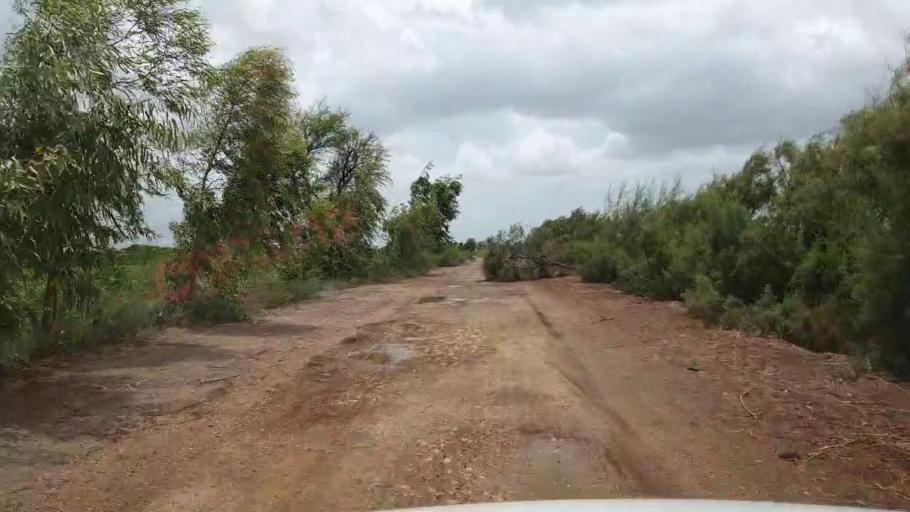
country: PK
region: Sindh
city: Kario
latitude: 24.7437
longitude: 68.5086
